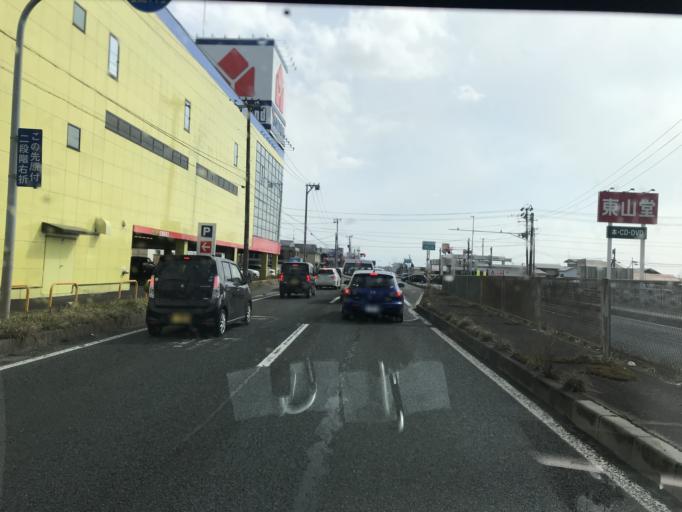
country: JP
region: Iwate
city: Kitakami
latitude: 39.3008
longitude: 141.1077
